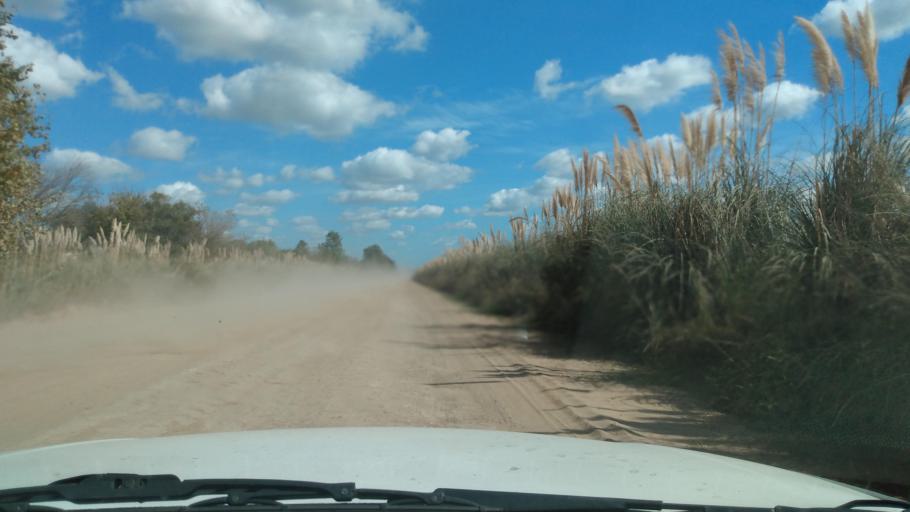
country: AR
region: Buenos Aires
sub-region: Partido de Navarro
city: Navarro
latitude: -34.9995
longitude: -59.3354
